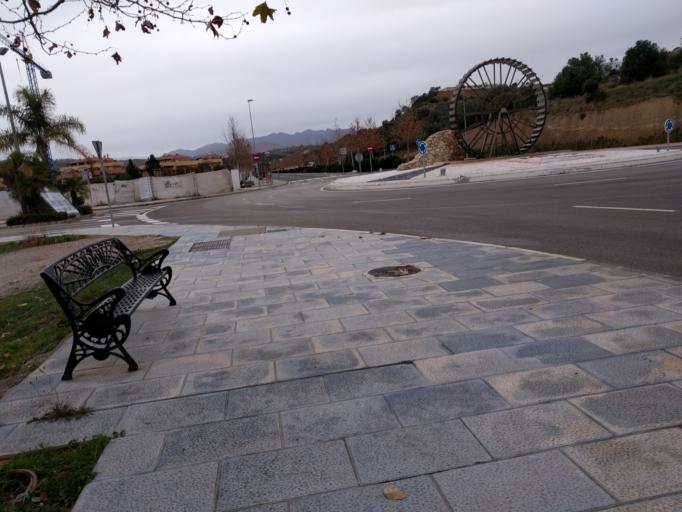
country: ES
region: Andalusia
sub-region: Provincia de Malaga
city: Fuengirola
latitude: 36.5074
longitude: -4.6839
